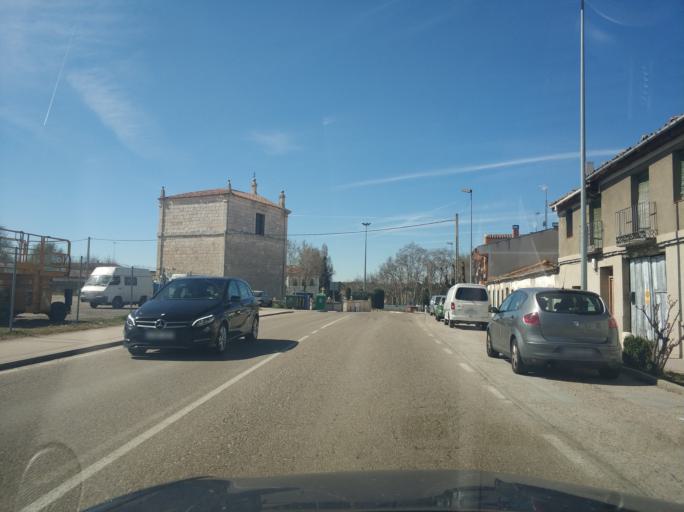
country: ES
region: Castille and Leon
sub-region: Provincia de Valladolid
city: Tudela de Duero
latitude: 41.5813
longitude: -4.5749
